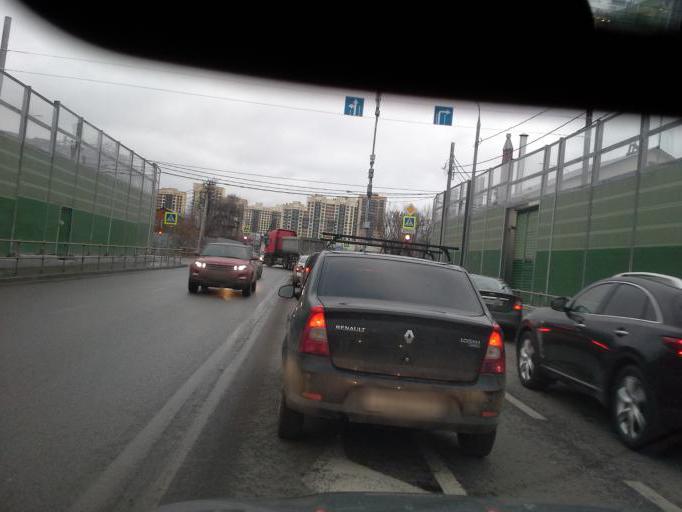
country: RU
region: Moscow
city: Novo-Peredelkino
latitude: 55.6314
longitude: 37.3354
